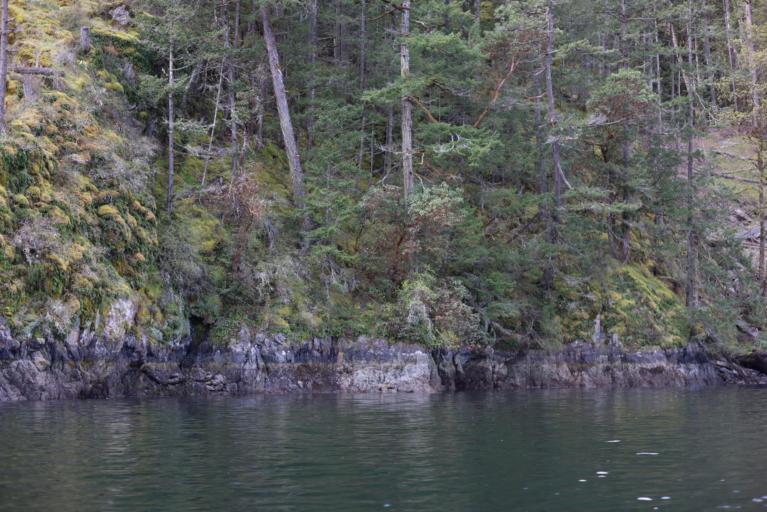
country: CA
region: British Columbia
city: Langford
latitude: 48.5092
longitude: -123.5481
